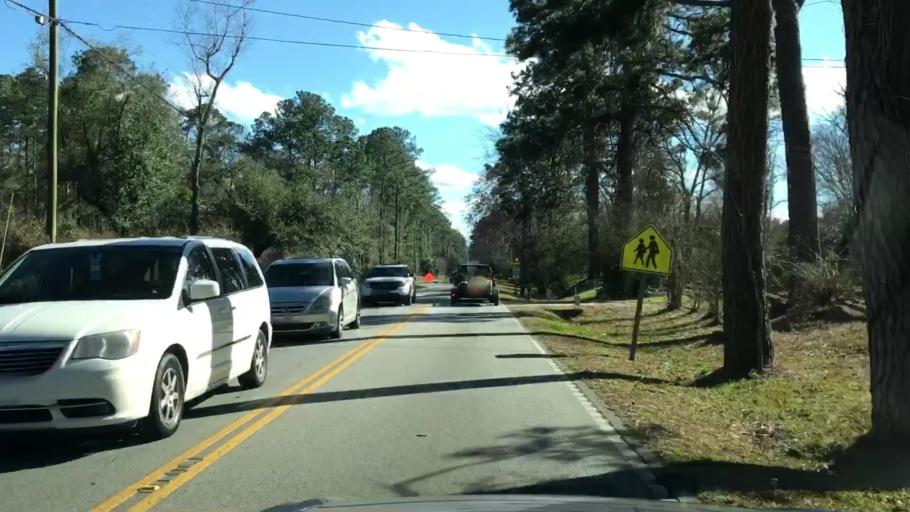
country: US
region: South Carolina
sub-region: Dorchester County
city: Summerville
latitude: 33.0319
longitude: -80.2455
